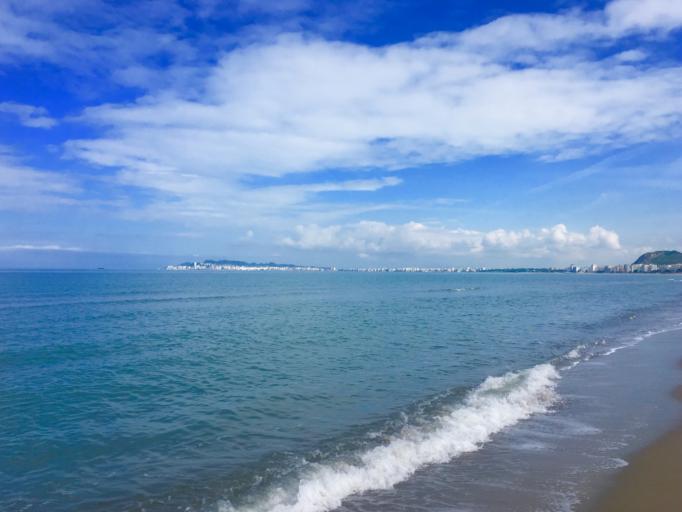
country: AL
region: Tirane
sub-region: Rrethi i Kavajes
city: Golem
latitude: 41.2524
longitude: 19.5190
